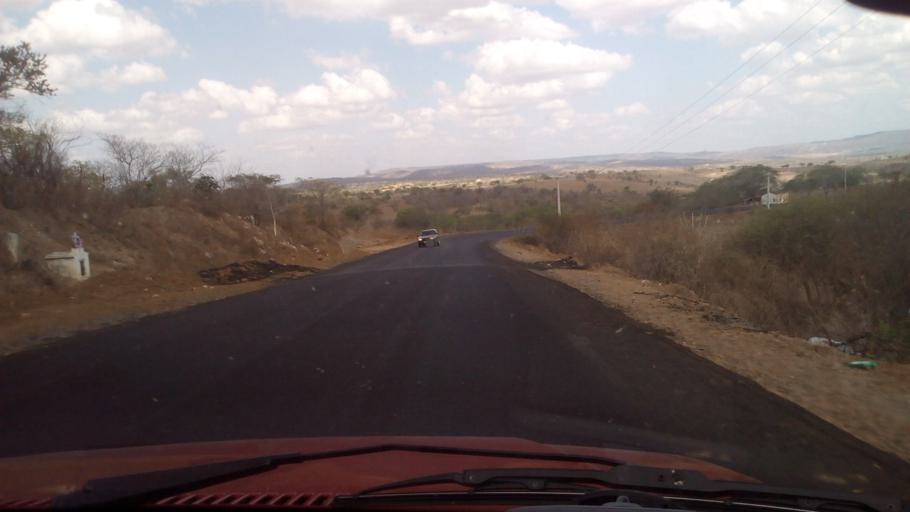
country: BR
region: Paraiba
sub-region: Cacimba De Dentro
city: Cacimba de Dentro
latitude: -6.6571
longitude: -35.7681
